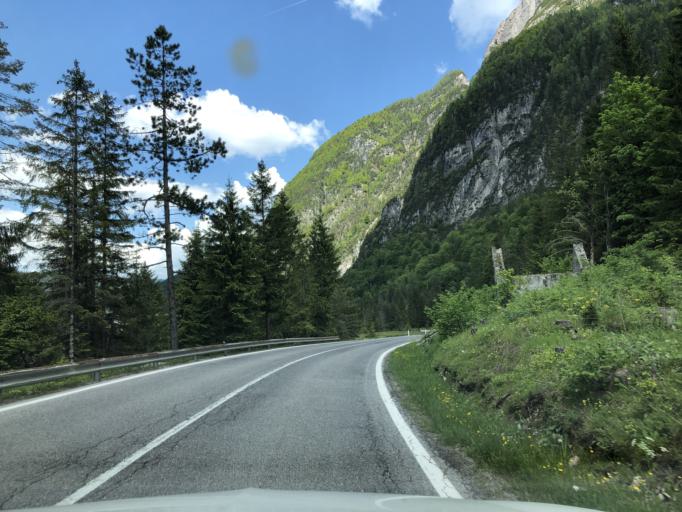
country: IT
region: Friuli Venezia Giulia
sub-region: Provincia di Udine
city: Tarvisio
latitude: 46.4482
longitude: 13.5736
